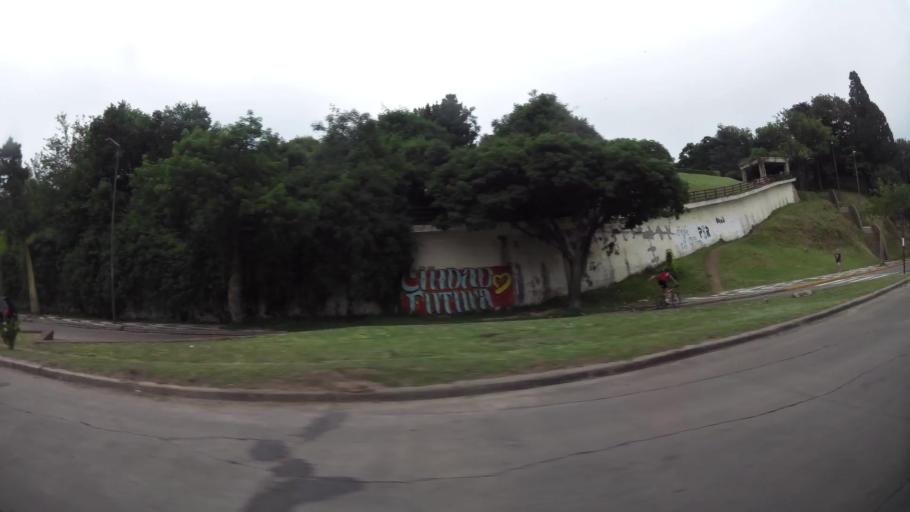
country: AR
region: Santa Fe
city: Granadero Baigorria
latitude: -32.9001
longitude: -60.6829
